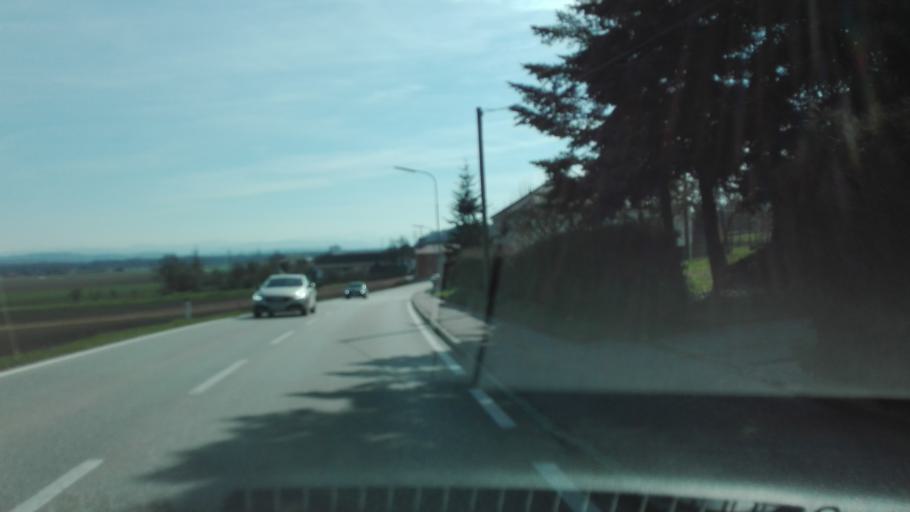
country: AT
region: Lower Austria
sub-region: Politischer Bezirk Amstetten
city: Ennsdorf
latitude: 48.2607
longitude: 14.5422
